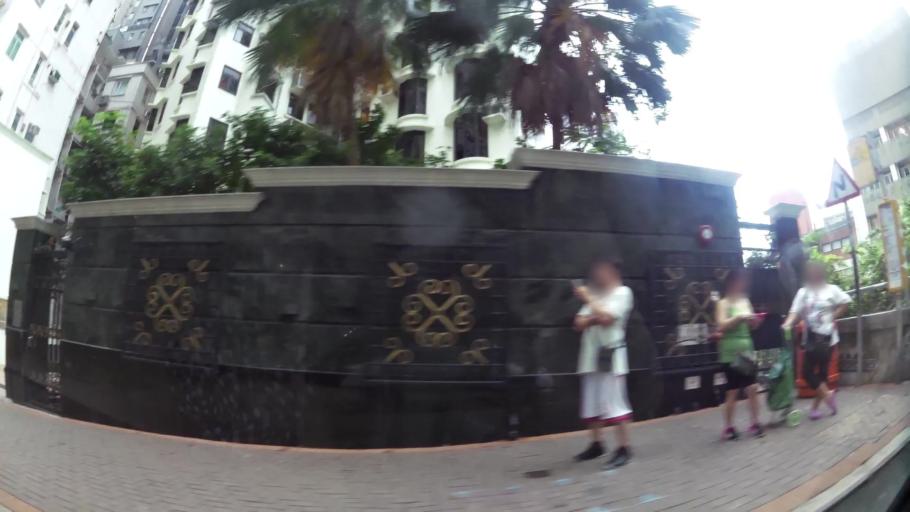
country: HK
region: Central and Western
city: Central
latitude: 22.2756
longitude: 114.1570
